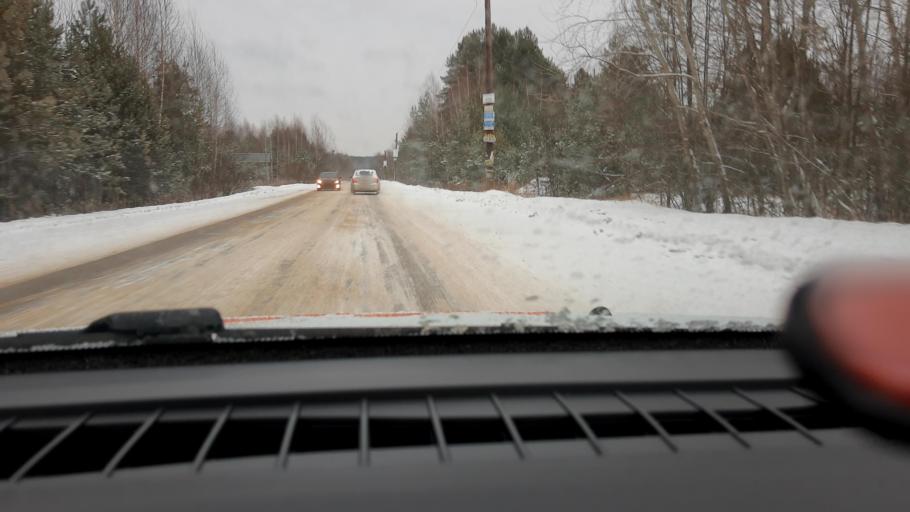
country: RU
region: Nizjnij Novgorod
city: Kstovo
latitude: 56.2779
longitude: 44.3456
